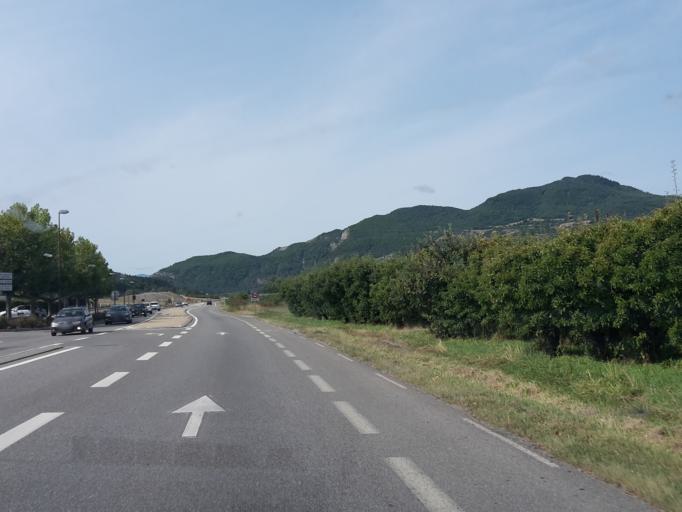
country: FR
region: Provence-Alpes-Cote d'Azur
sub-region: Departement des Hautes-Alpes
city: Tallard
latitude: 44.4573
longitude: 6.0485
